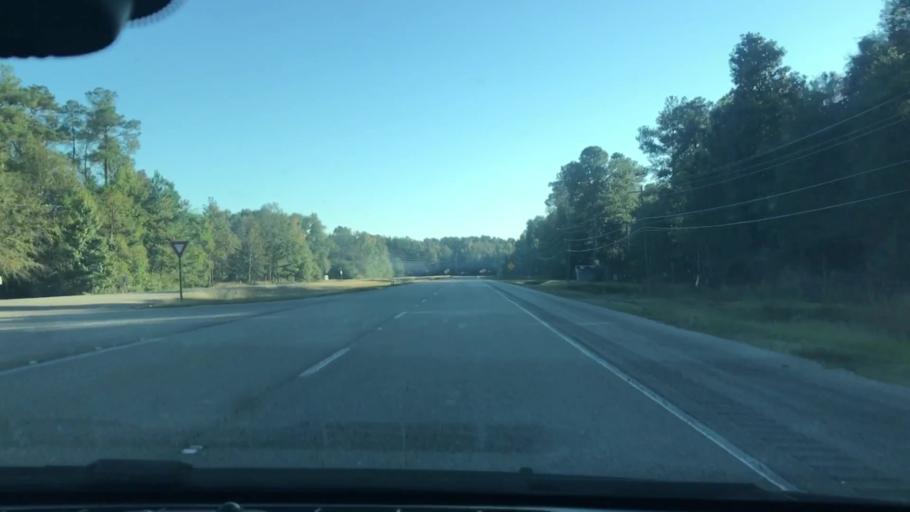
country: US
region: Louisiana
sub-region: Washington Parish
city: Bogalusa
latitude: 30.6141
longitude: -89.8991
